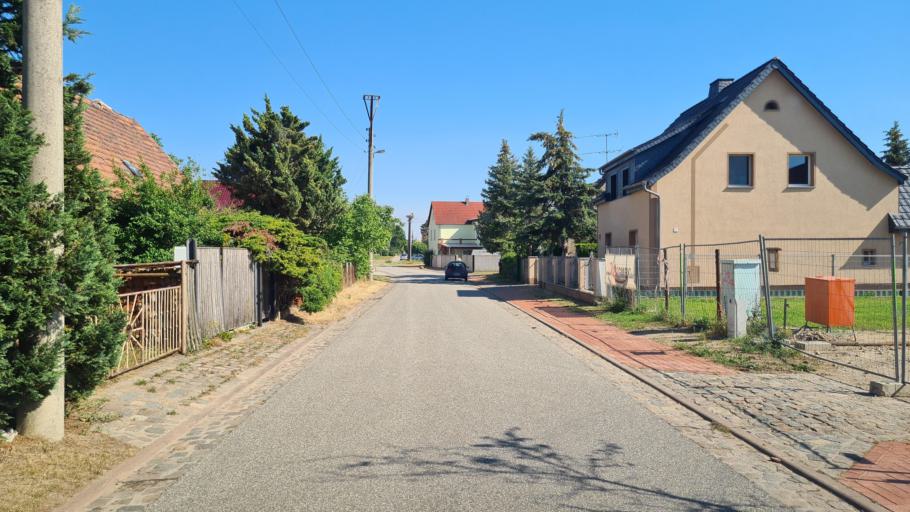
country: DE
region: Saxony-Anhalt
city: Annaburg
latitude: 51.6997
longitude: 12.9919
